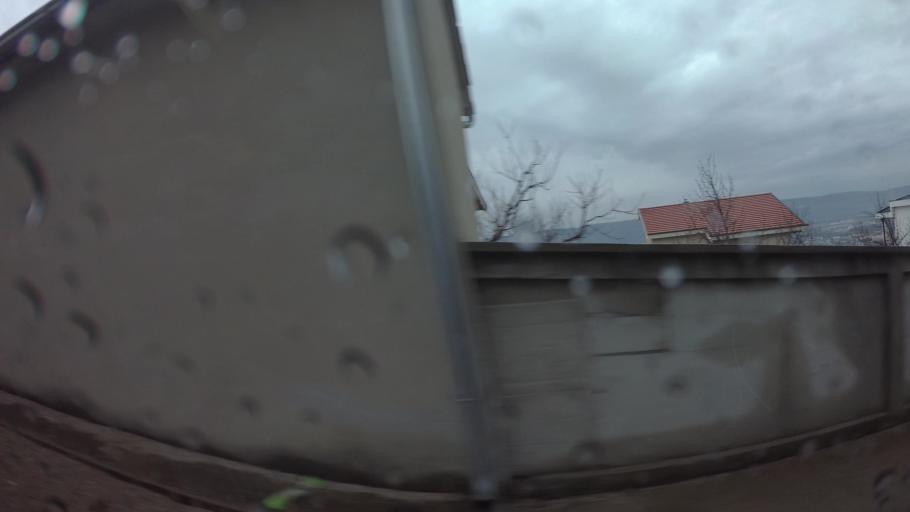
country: BA
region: Federation of Bosnia and Herzegovina
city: Rodoc
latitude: 43.3056
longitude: 17.8486
